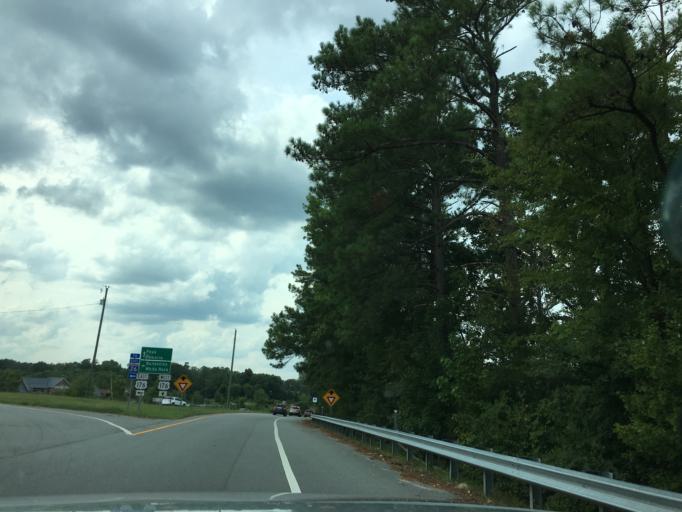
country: US
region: South Carolina
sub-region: Richland County
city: Lake Murray of Richland
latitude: 34.1481
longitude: -81.2377
